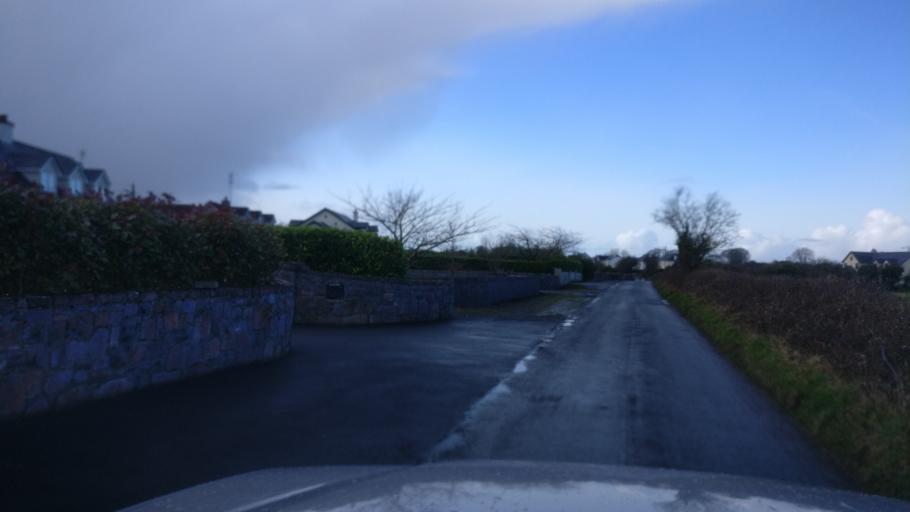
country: IE
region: Connaught
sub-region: County Galway
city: Oranmore
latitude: 53.2654
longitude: -8.8754
